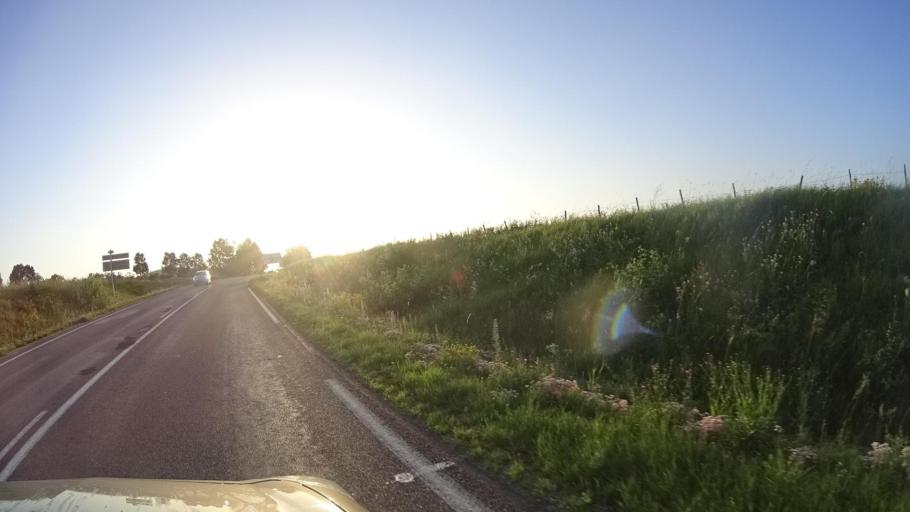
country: FR
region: Franche-Comte
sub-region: Departement du Doubs
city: Doubs
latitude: 46.9082
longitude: 6.2647
